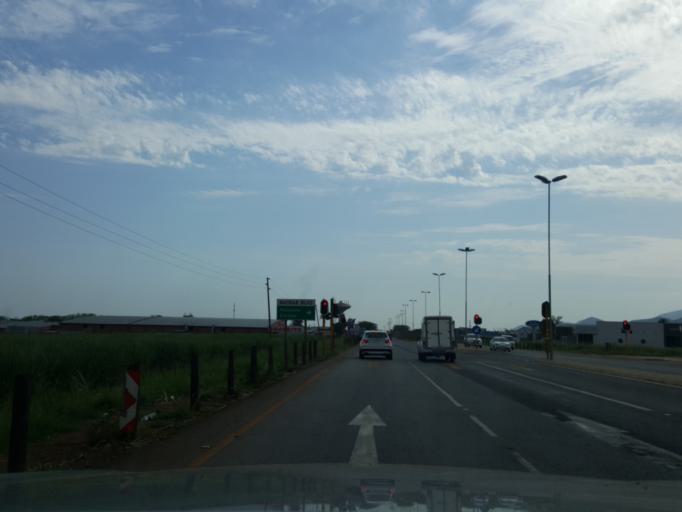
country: SZ
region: Hhohho
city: Ntfonjeni
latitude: -25.5020
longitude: 31.5035
